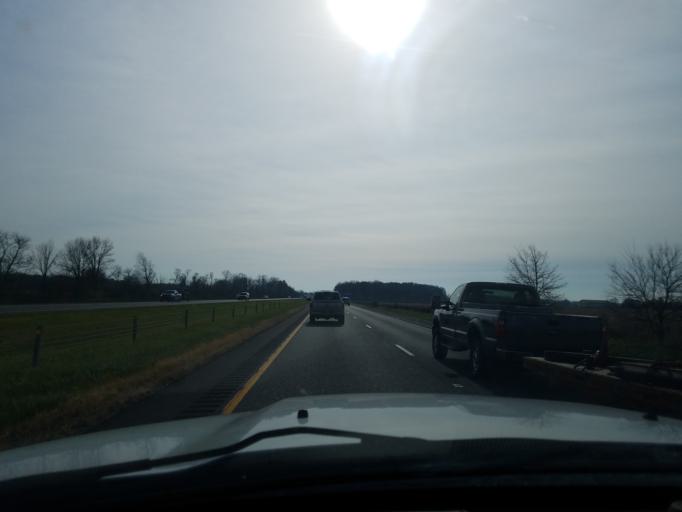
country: US
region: Indiana
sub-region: Delaware County
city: Daleville
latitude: 40.1540
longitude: -85.5671
